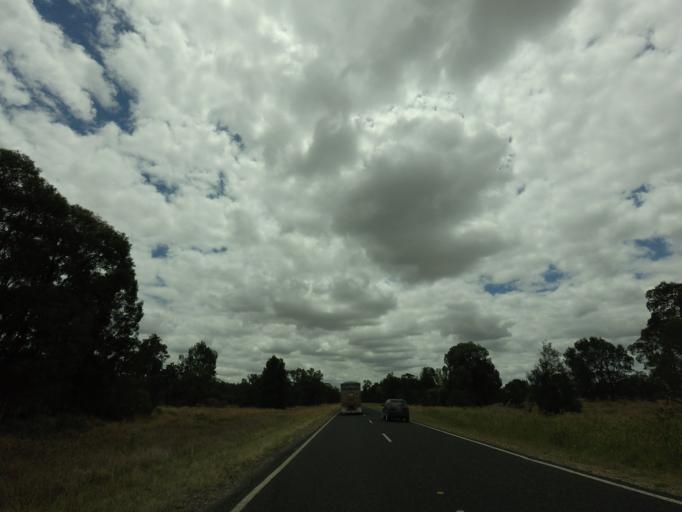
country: AU
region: Queensland
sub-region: Goondiwindi
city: Goondiwindi
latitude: -28.4268
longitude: 150.3026
